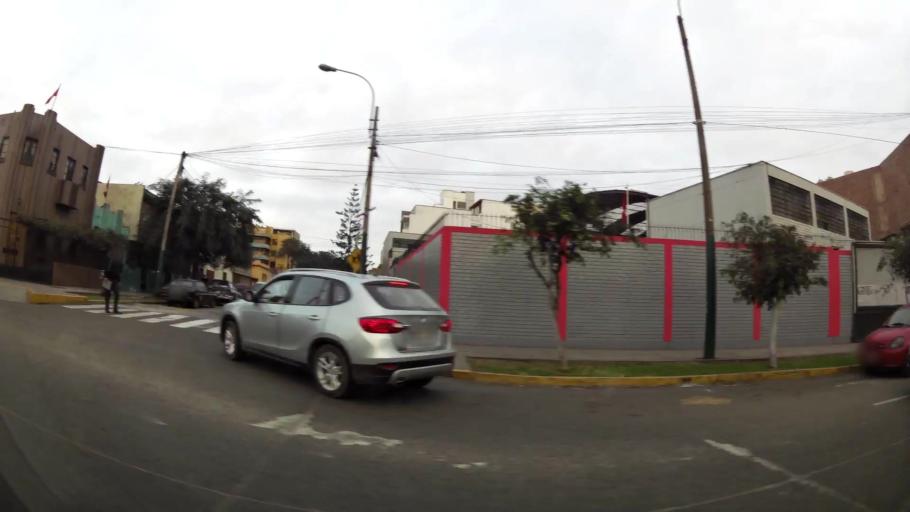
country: PE
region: Lima
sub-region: Lima
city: San Isidro
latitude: -12.0906
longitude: -77.0698
